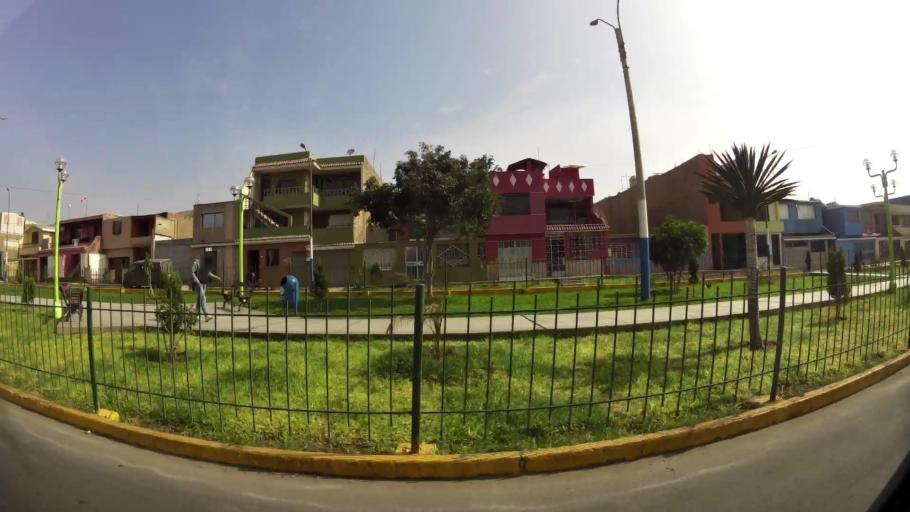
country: PE
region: Lima
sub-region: Lima
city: Santa Rosa
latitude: -11.7784
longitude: -77.1646
